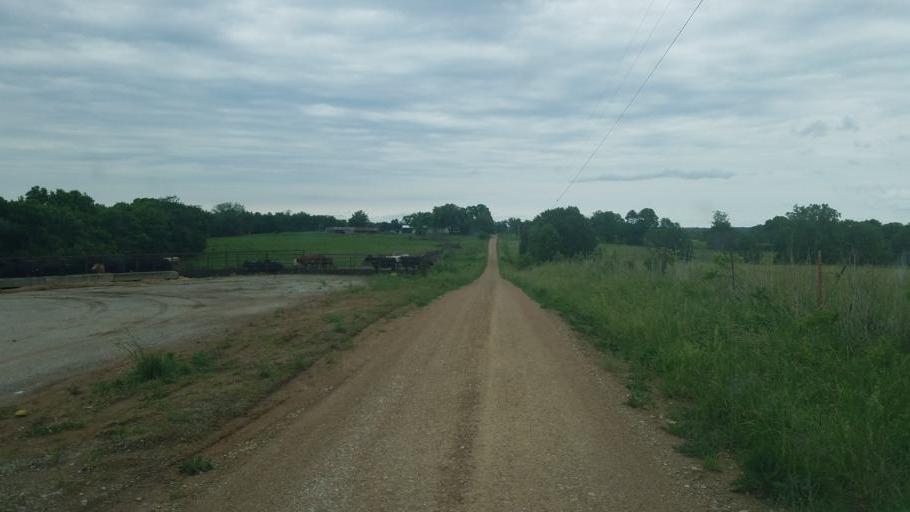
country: US
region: Missouri
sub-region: Moniteau County
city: California
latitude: 38.6013
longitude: -92.6474
